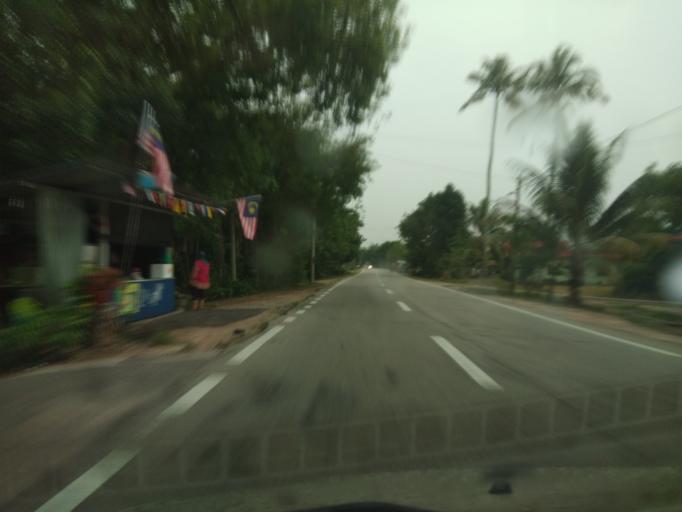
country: MY
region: Penang
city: Kepala Batas
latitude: 5.4993
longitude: 100.3960
